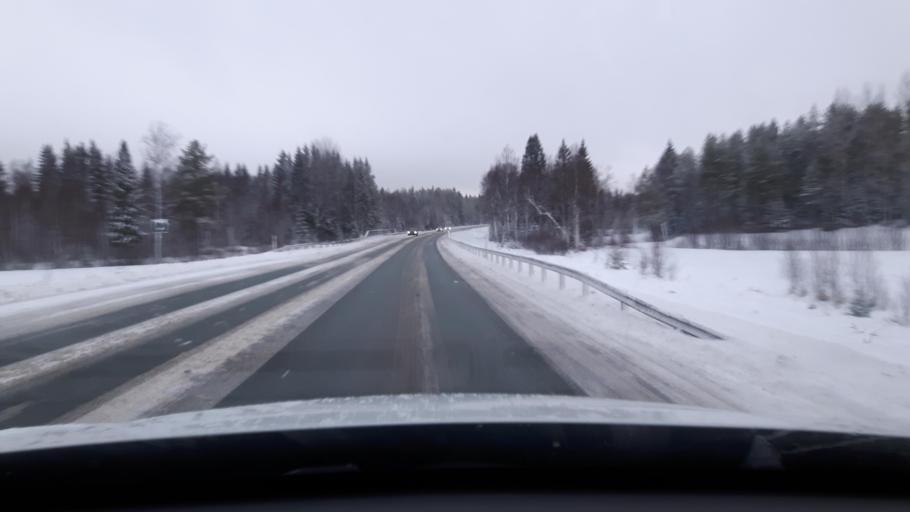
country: SE
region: Vaesterbotten
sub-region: Robertsfors Kommun
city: Robertsfors
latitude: 64.0322
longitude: 20.8418
